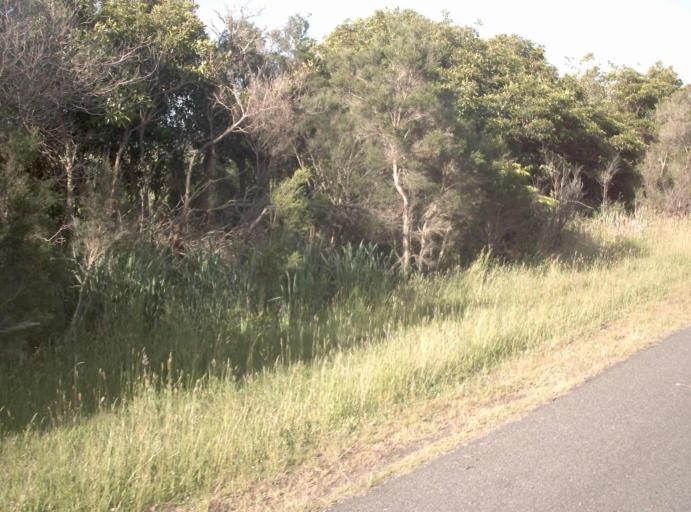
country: AU
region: Victoria
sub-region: Bass Coast
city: North Wonthaggi
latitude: -38.6265
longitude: 145.7244
